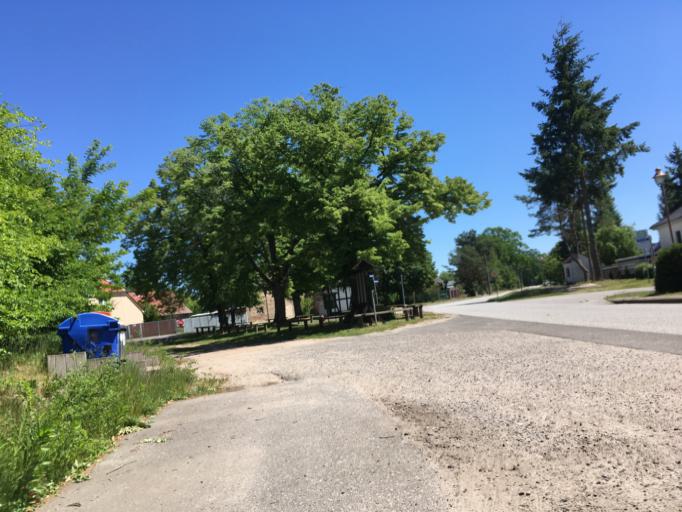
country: DE
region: Brandenburg
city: Zehdenick
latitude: 52.9833
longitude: 13.3792
